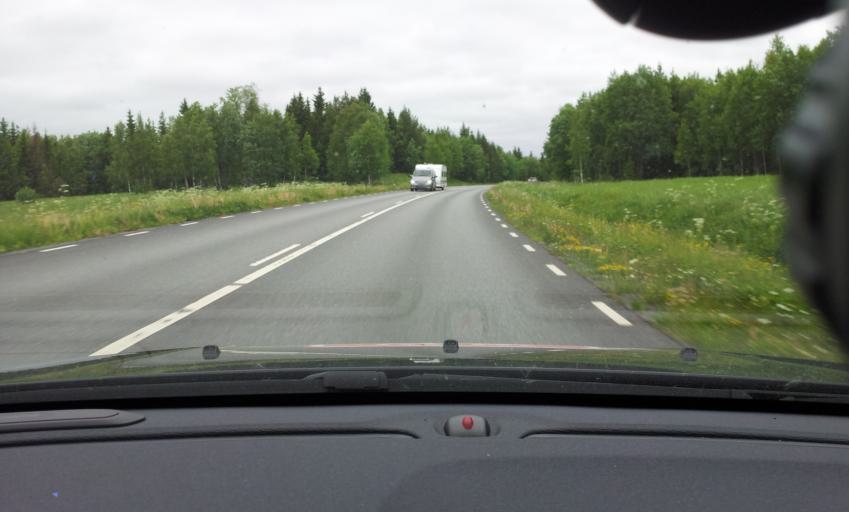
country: SE
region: Jaemtland
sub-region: Krokoms Kommun
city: Krokom
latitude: 63.0785
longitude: 14.2914
